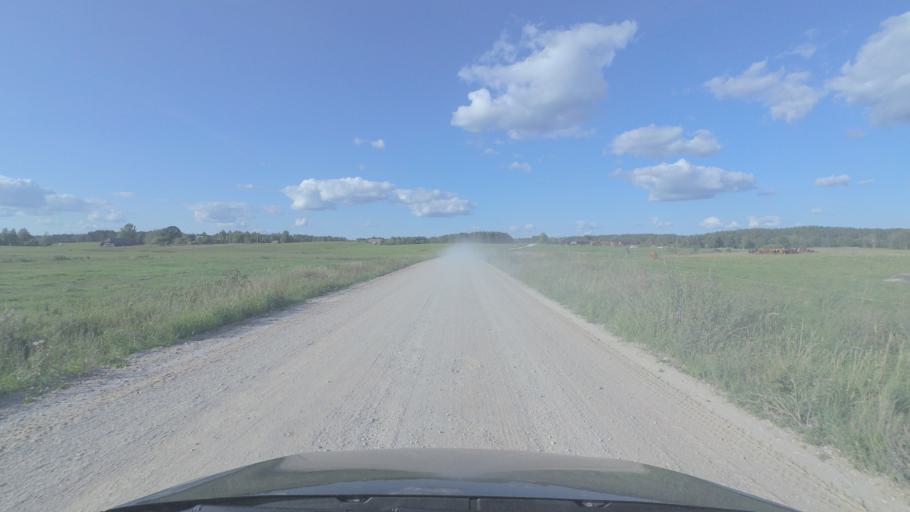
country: LT
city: Pabrade
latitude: 55.1337
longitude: 25.7073
